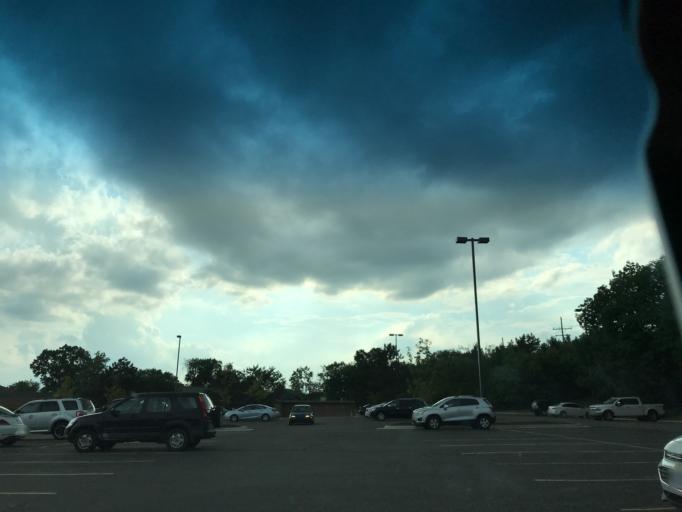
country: US
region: Michigan
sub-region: Washtenaw County
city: Ann Arbor
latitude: 42.2455
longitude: -83.7414
